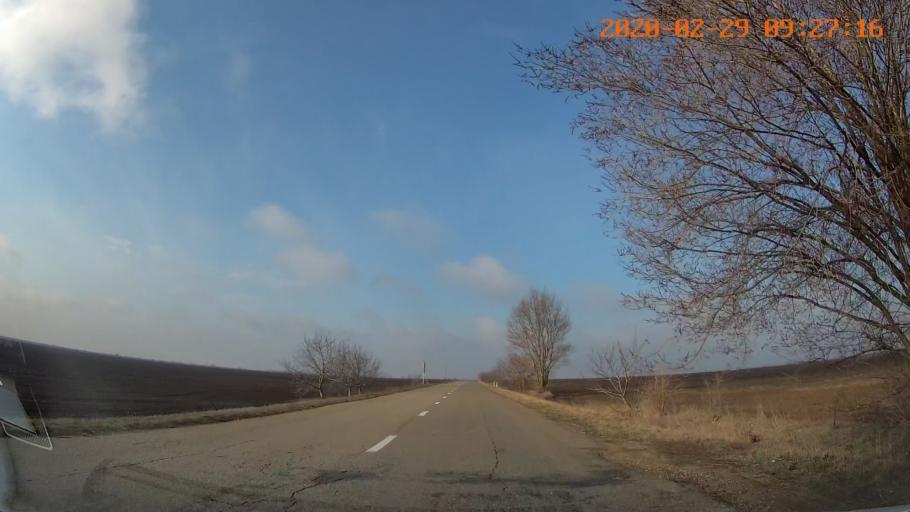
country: MD
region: Telenesti
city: Pervomaisc
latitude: 46.6986
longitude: 29.9447
